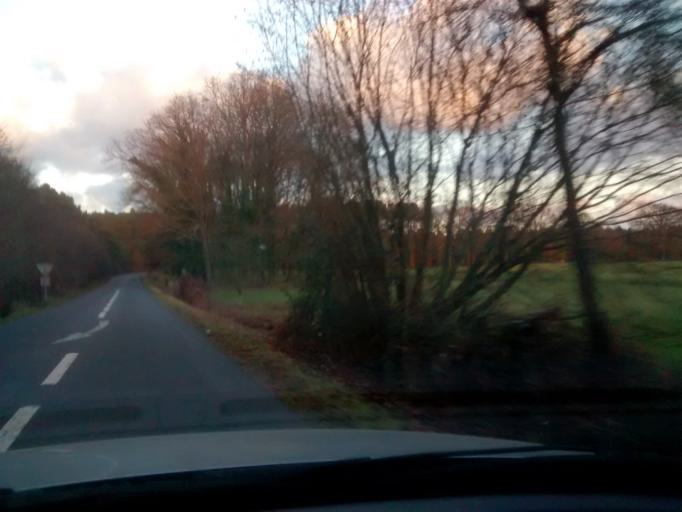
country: FR
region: Pays de la Loire
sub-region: Departement de la Sarthe
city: Brette-les-Pins
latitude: 47.9498
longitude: 0.3570
